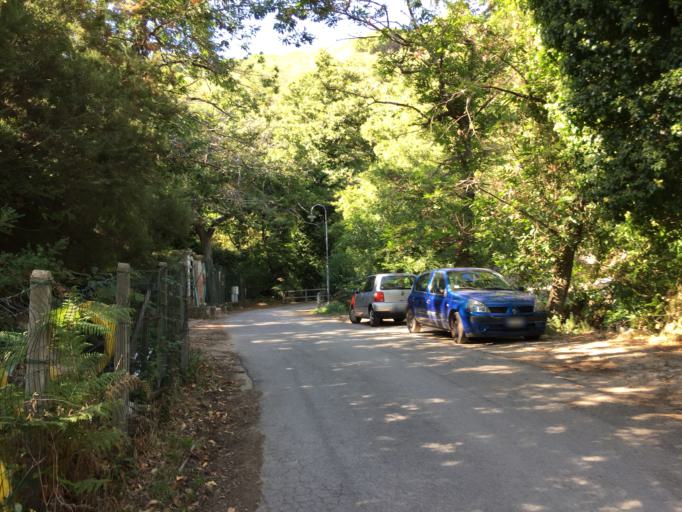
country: IT
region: Tuscany
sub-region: Provincia di Livorno
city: Marciana
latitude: 42.7868
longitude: 10.1661
